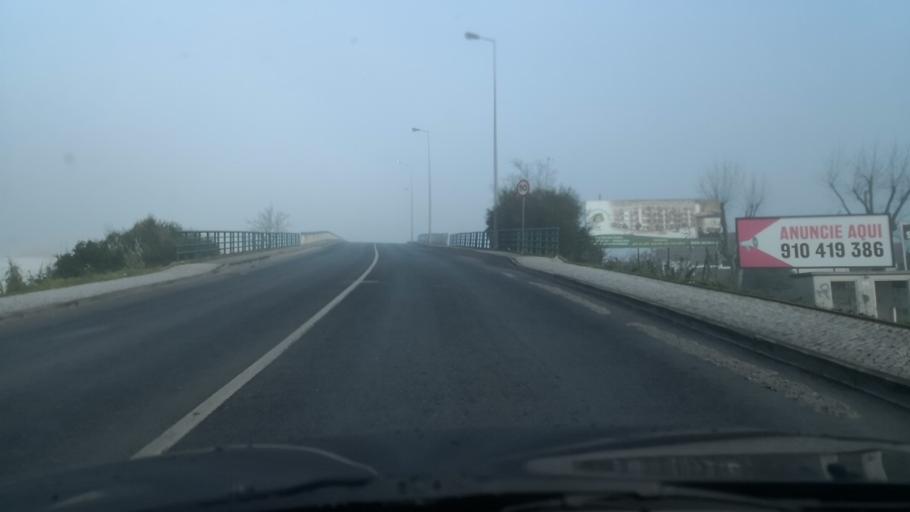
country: PT
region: Setubal
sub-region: Palmela
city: Pinhal Novo
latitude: 38.6289
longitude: -8.9178
